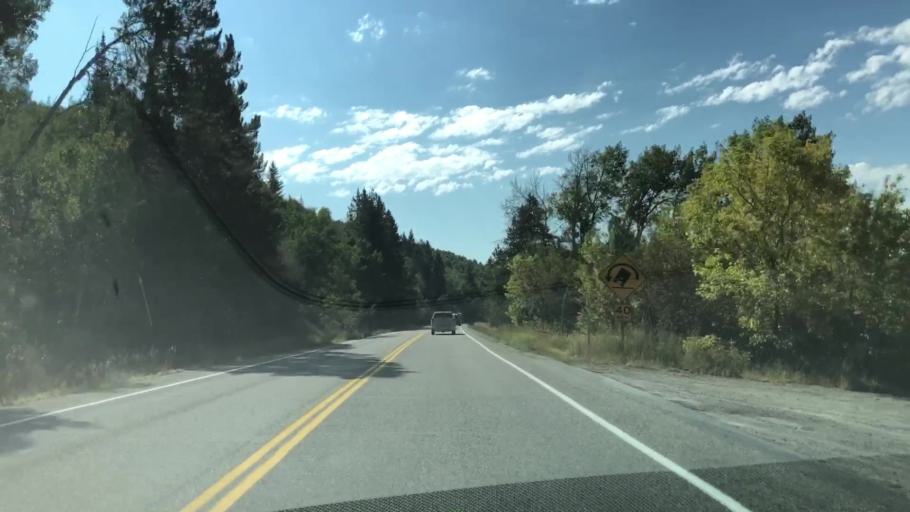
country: US
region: Idaho
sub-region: Teton County
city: Victor
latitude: 43.3243
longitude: -111.1674
